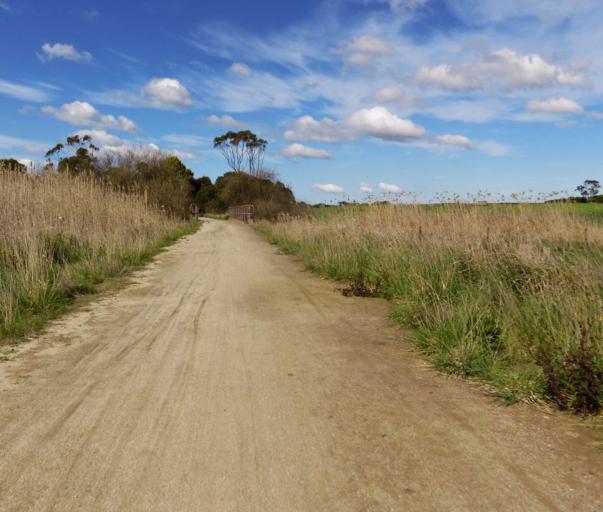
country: AU
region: Victoria
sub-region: Baw Baw
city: Warragul
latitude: -38.5113
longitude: 145.9410
